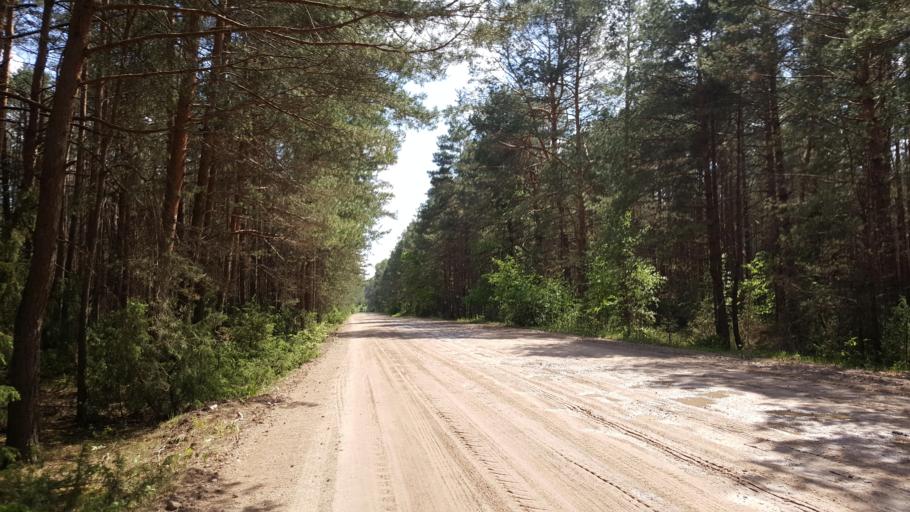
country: BY
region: Brest
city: Kamyanyets
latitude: 52.4347
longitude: 23.9724
